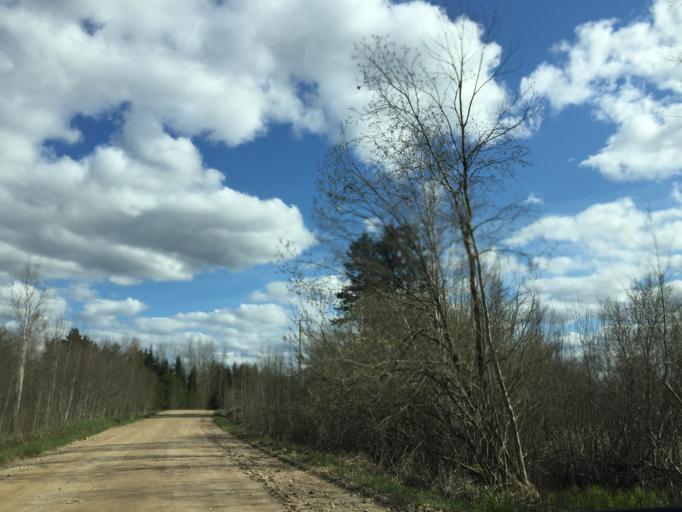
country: LV
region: Rezekne
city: Rezekne
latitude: 56.6539
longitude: 27.2831
